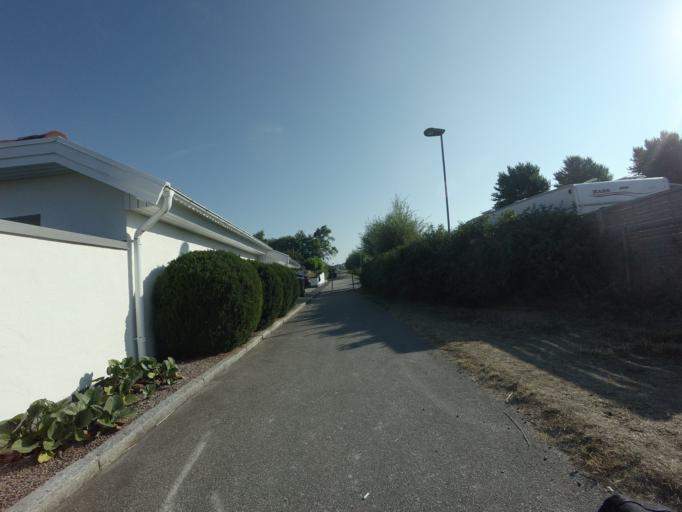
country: SE
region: Skane
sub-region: Trelleborgs Kommun
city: Trelleborg
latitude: 55.3632
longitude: 13.2068
